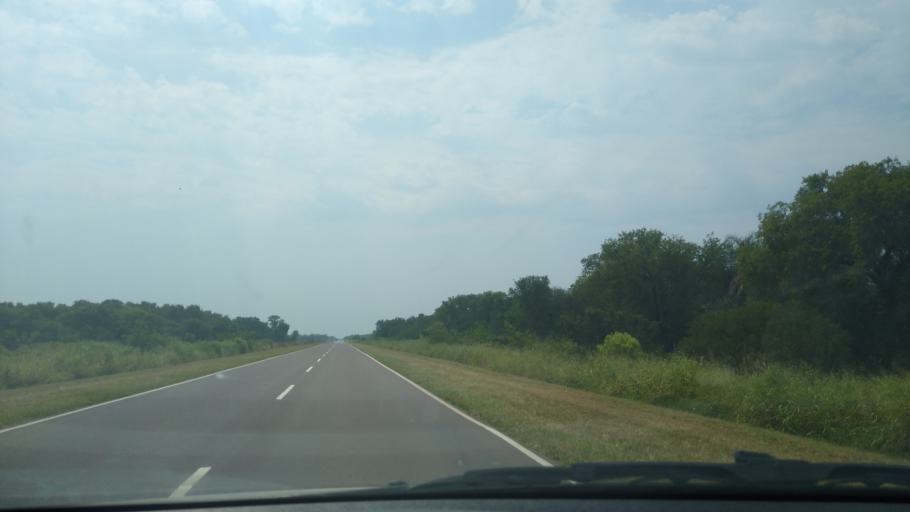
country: AR
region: Chaco
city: La Eduvigis
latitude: -27.0417
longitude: -58.9635
